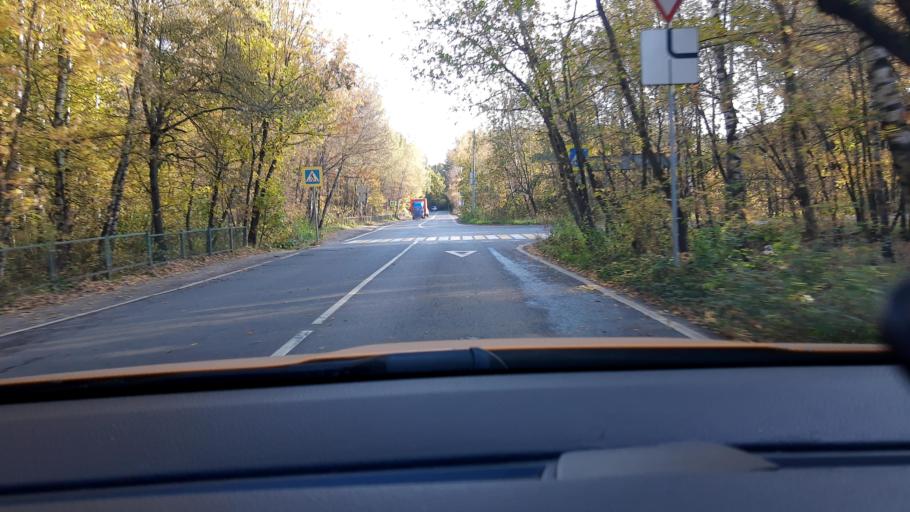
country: RU
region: Moskovskaya
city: Bogorodskoye
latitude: 55.8284
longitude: 37.7466
